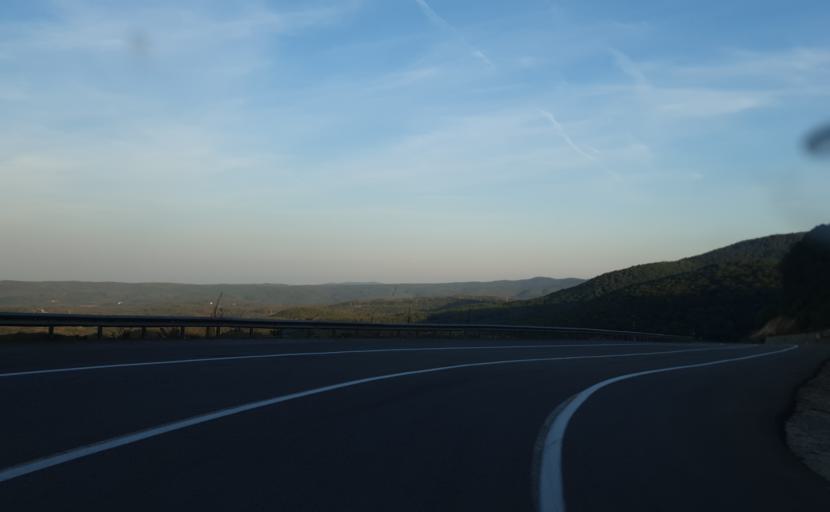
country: TR
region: Kirklareli
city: Sergen
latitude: 41.8152
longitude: 27.7447
